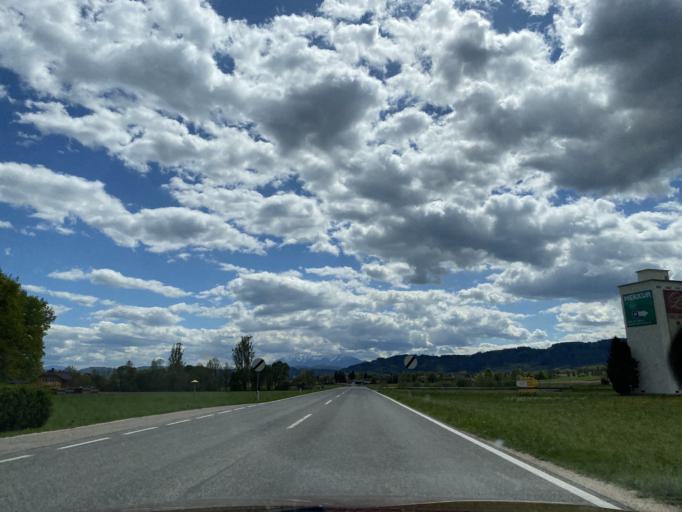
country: AT
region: Carinthia
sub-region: Politischer Bezirk Wolfsberg
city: Sankt Andrae
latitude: 46.7985
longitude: 14.8277
